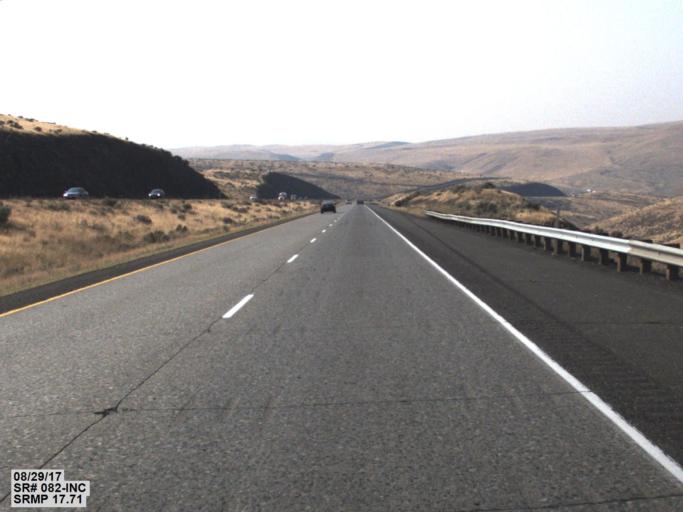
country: US
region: Washington
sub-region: Yakima County
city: Terrace Heights
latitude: 46.7663
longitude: -120.3784
